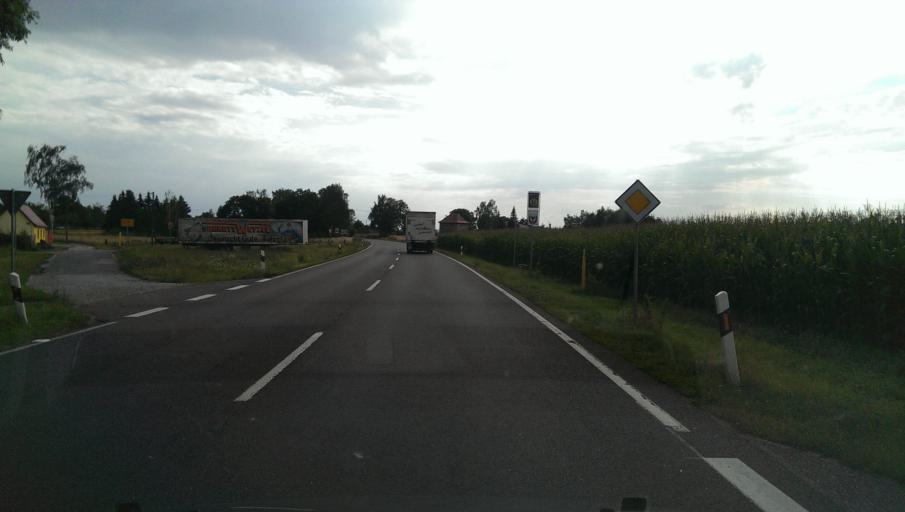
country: DE
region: Saxony
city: Elstertrebnitz
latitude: 51.1367
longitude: 12.2277
